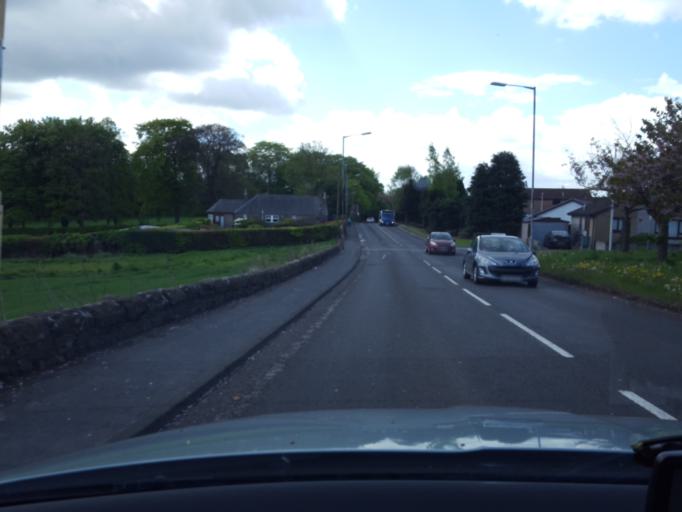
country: GB
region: Scotland
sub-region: Angus
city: Brechin
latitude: 56.7392
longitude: -2.6558
